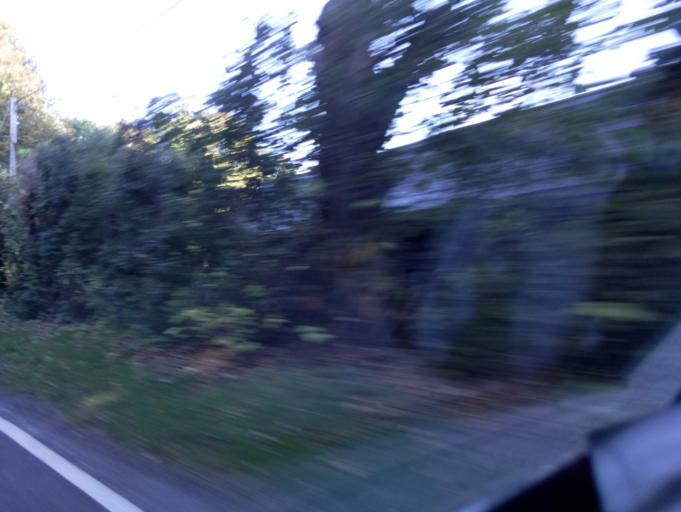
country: GB
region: England
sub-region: Hampshire
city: Swanmore
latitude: 50.9560
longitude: -1.1389
